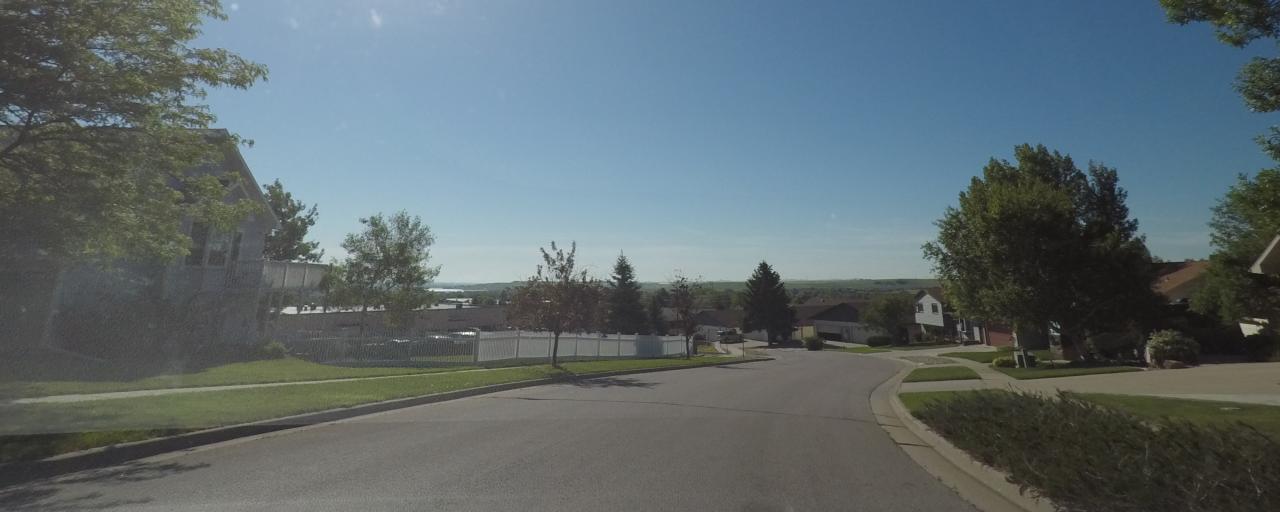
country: US
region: South Dakota
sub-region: Pennington County
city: Rapid City
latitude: 44.0505
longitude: -103.2263
